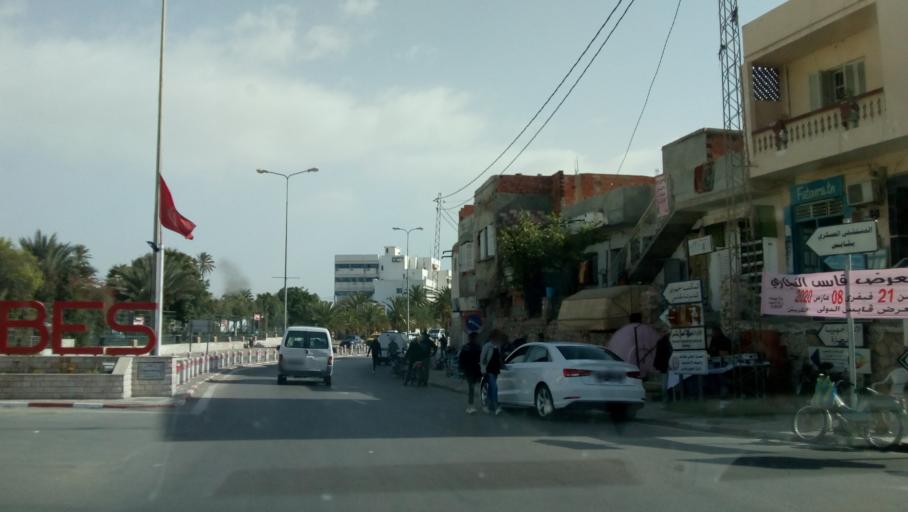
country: TN
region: Qabis
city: Gabes
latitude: 33.8839
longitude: 10.0872
